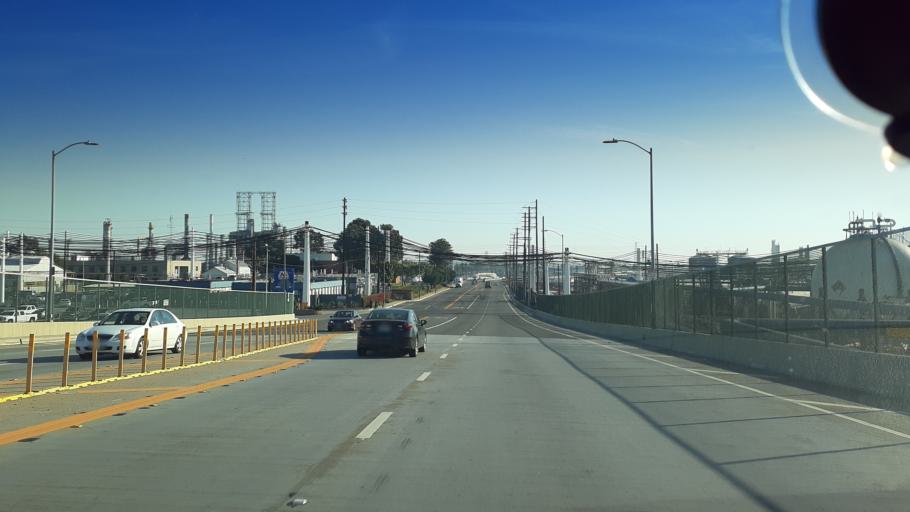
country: US
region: California
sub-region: Los Angeles County
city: Long Beach
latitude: 33.7914
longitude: -118.2372
